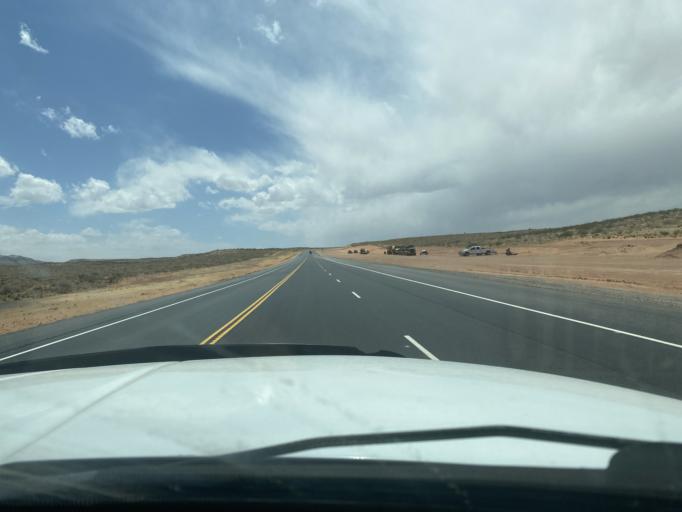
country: US
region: Utah
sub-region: Washington County
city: Hurricane
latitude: 37.1194
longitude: -113.3432
